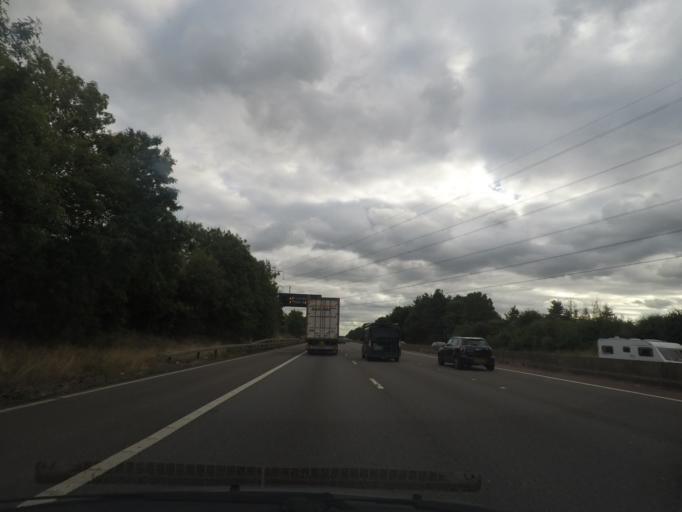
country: GB
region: England
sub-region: Leicestershire
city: Lutterworth
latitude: 52.4736
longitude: -1.1921
